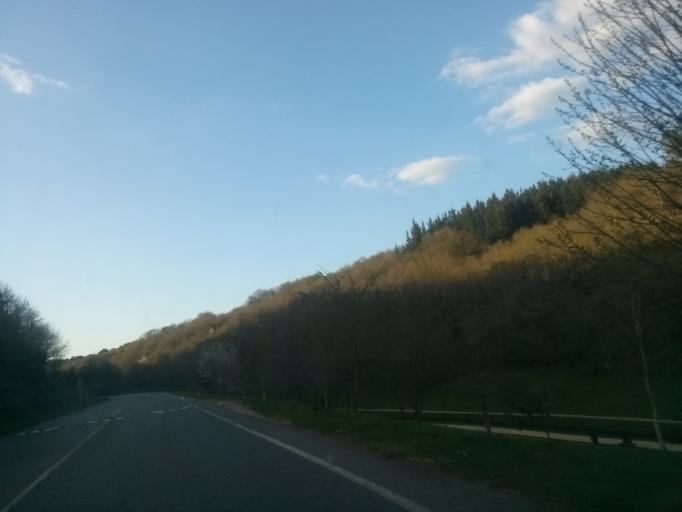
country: ES
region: Galicia
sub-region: Provincia de Lugo
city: Lugo
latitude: 42.9985
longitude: -7.5311
